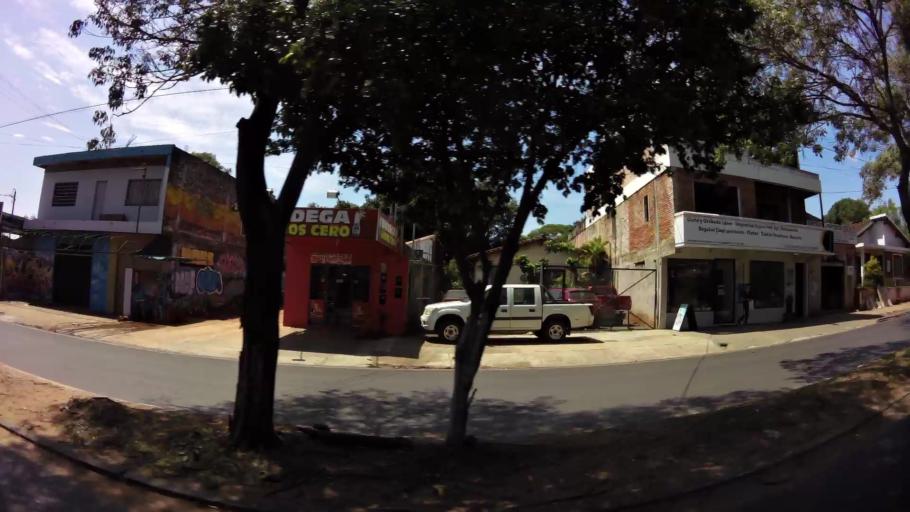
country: PY
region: Central
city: San Lorenzo
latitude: -25.3576
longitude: -57.5144
